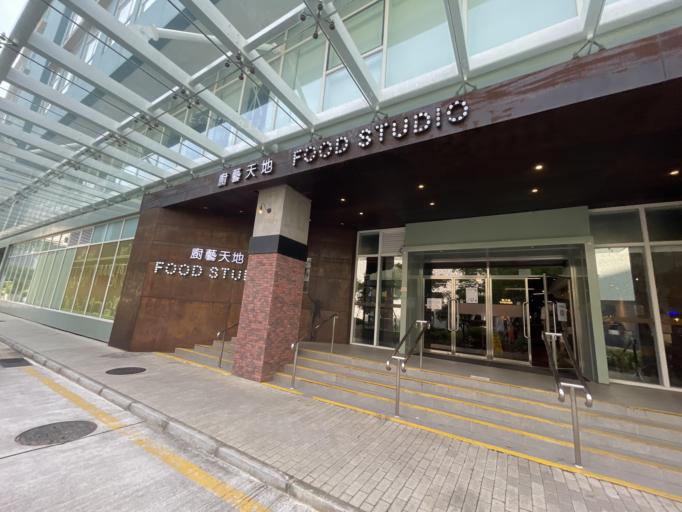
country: MO
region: Macau
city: Macau
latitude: 22.1515
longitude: 113.5666
